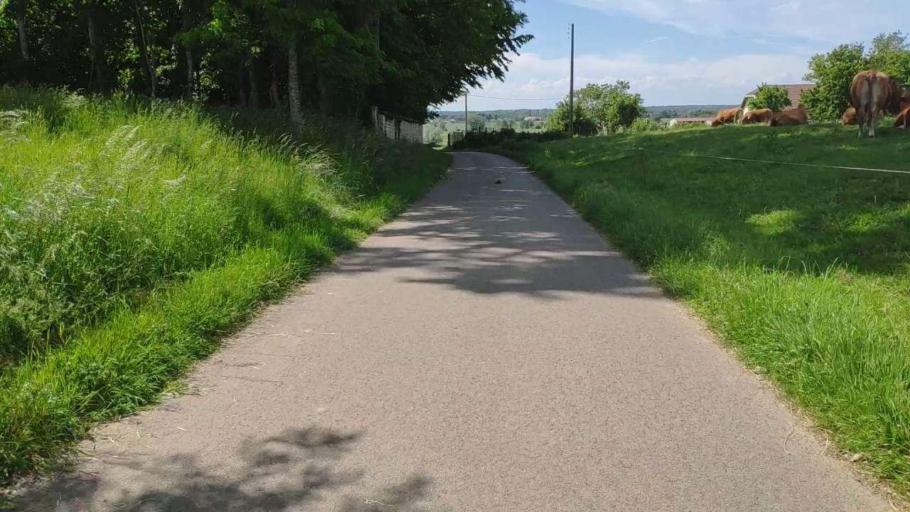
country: FR
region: Franche-Comte
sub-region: Departement du Jura
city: Bletterans
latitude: 46.7317
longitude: 5.5028
